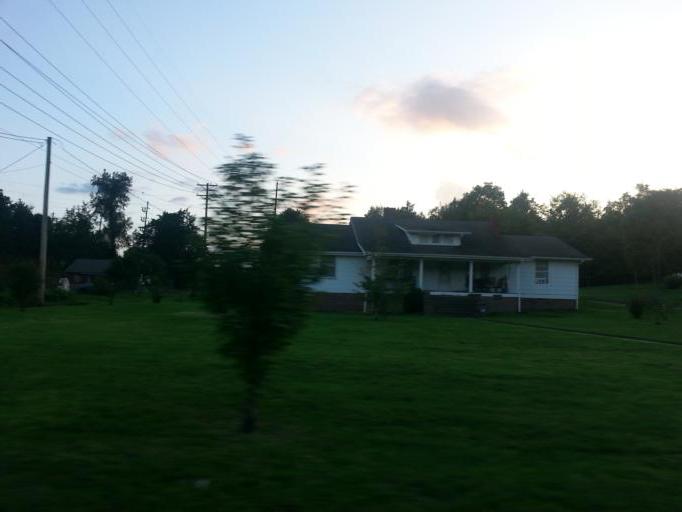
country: US
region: Tennessee
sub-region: Union County
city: Luttrell
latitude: 36.2093
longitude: -83.7453
